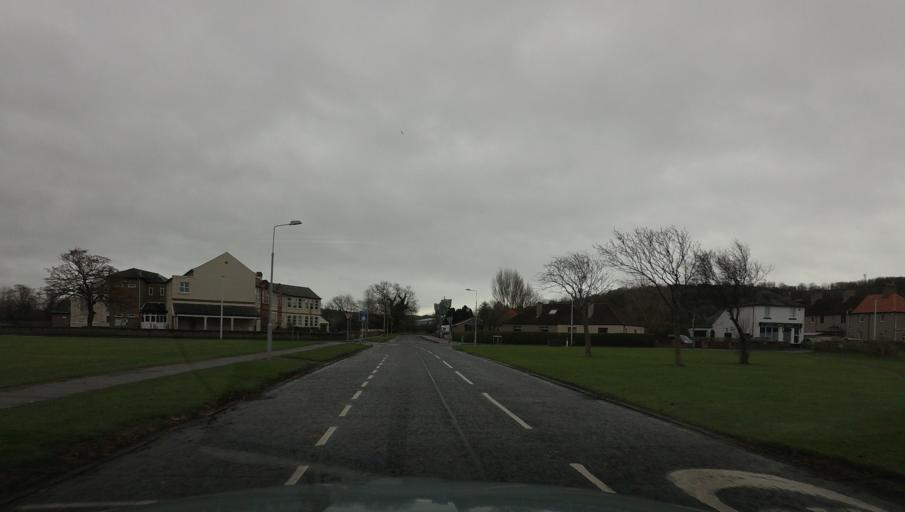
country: GB
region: Scotland
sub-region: Fife
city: Inverkeithing
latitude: 56.0392
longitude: -3.4106
